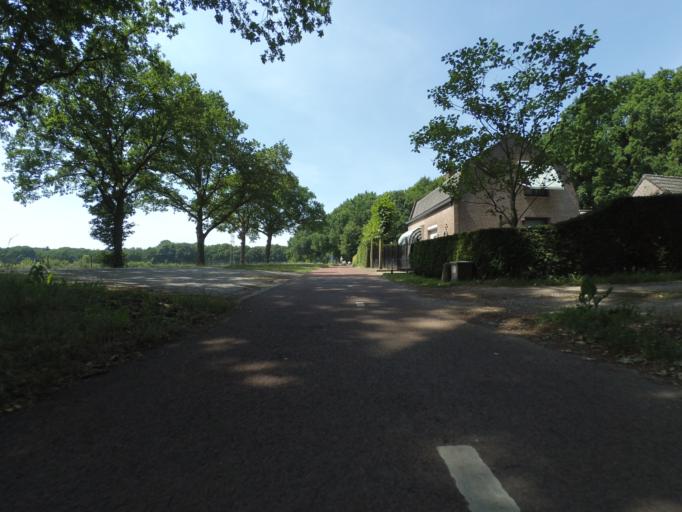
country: NL
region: North Brabant
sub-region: Gemeente Bergen op Zoom
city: Bergen op Zoom
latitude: 51.4741
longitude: 4.3253
